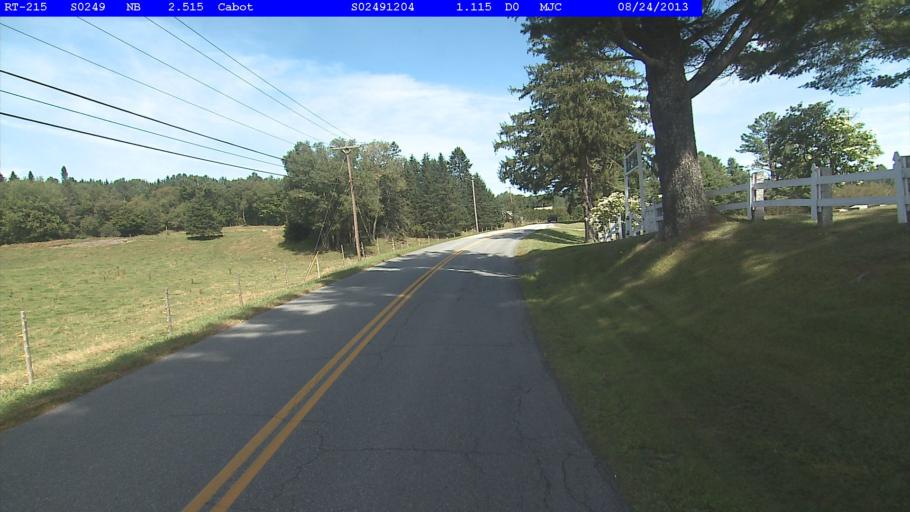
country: US
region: Vermont
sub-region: Caledonia County
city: Hardwick
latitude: 44.3833
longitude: -72.3341
